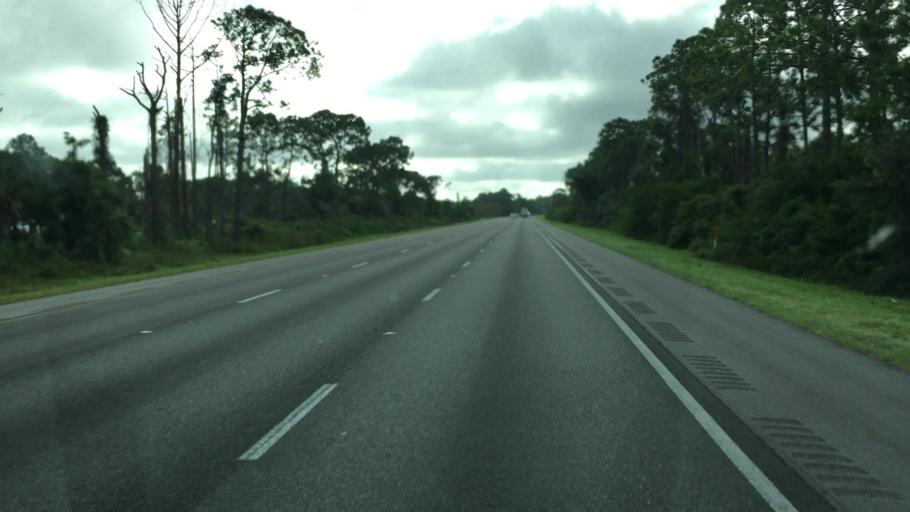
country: US
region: Florida
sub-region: Volusia County
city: Samsula-Spruce Creek
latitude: 29.0736
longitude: -81.0130
